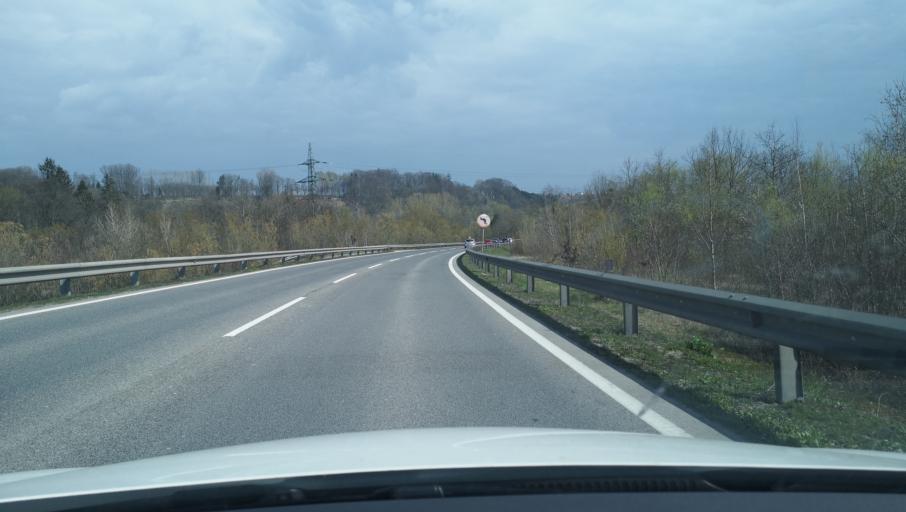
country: AT
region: Lower Austria
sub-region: Politischer Bezirk Amstetten
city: Winklarn
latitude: 48.1125
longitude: 14.8388
